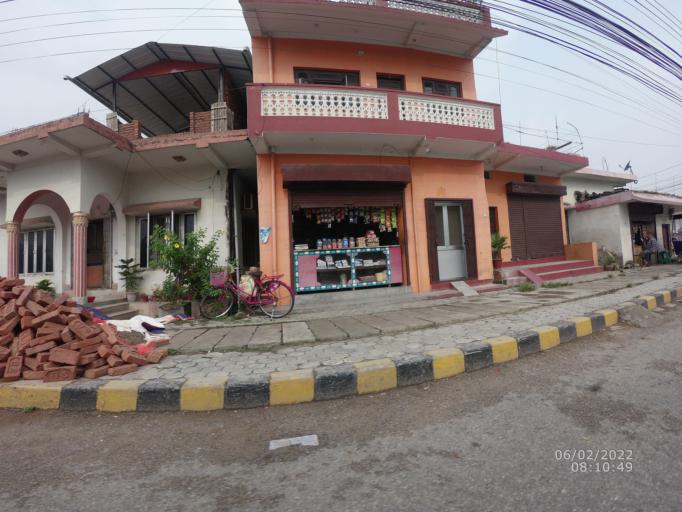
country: NP
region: Western Region
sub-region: Lumbini Zone
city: Bhairahawa
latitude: 27.4940
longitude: 83.4597
